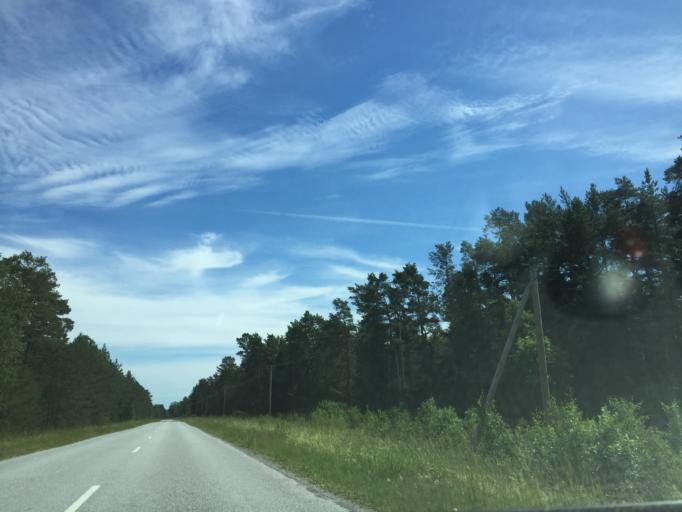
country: LV
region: Rojas
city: Roja
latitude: 57.5827
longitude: 22.6202
